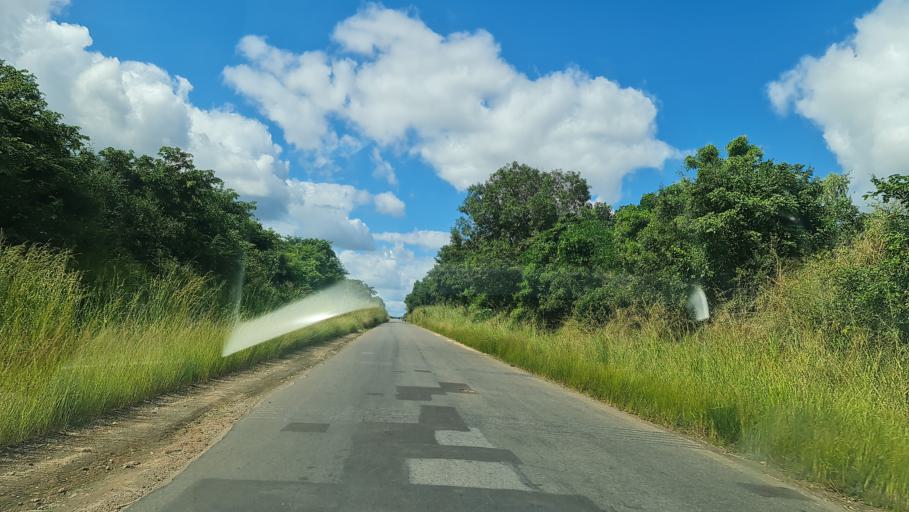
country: MZ
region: Zambezia
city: Quelimane
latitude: -17.5252
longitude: 36.2750
